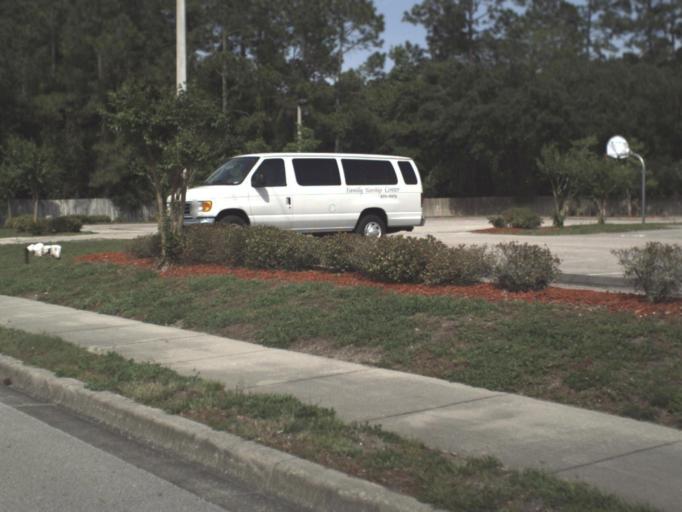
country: US
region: Florida
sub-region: Saint Johns County
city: Saint Augustine South
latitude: 29.8387
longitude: -81.3680
